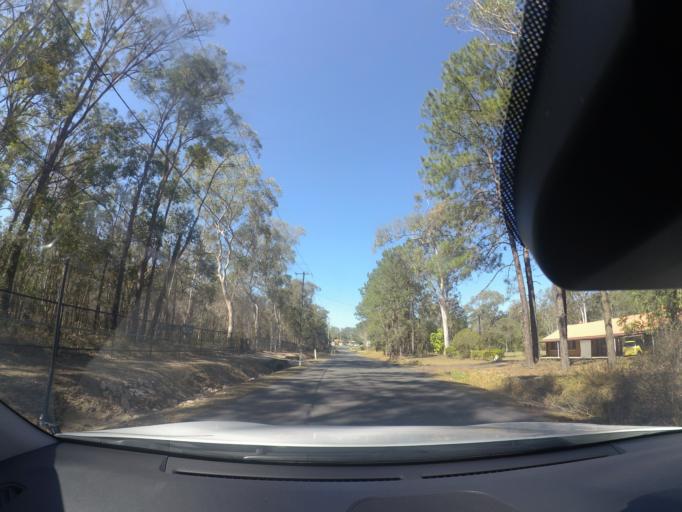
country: AU
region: Queensland
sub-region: Logan
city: Woodridge
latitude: -27.6405
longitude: 153.0942
